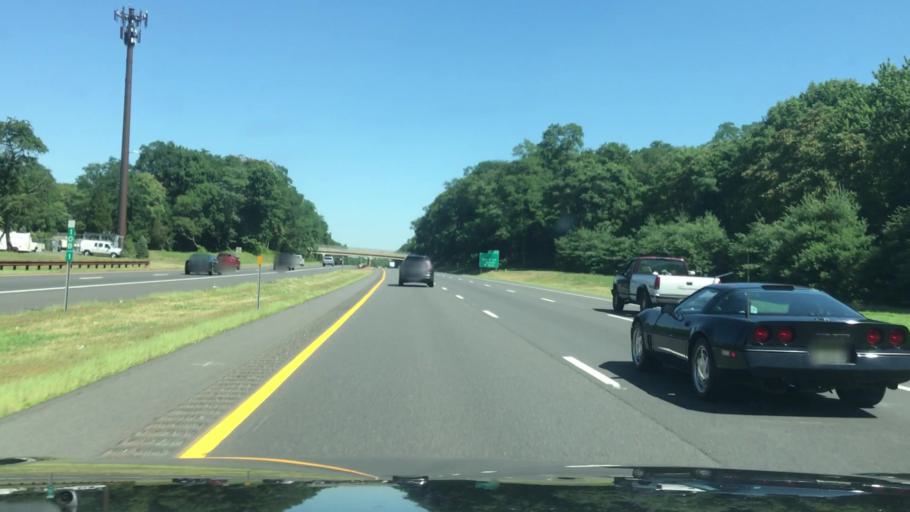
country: US
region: New Jersey
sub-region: Monmouth County
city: Tinton Falls
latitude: 40.3076
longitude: -74.0938
